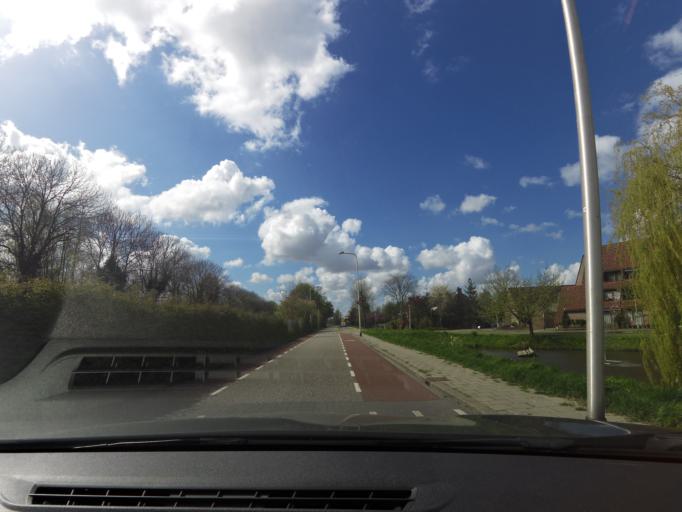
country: NL
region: South Holland
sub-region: Gemeente Albrandswaard
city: Rhoon
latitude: 51.8590
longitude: 4.4122
